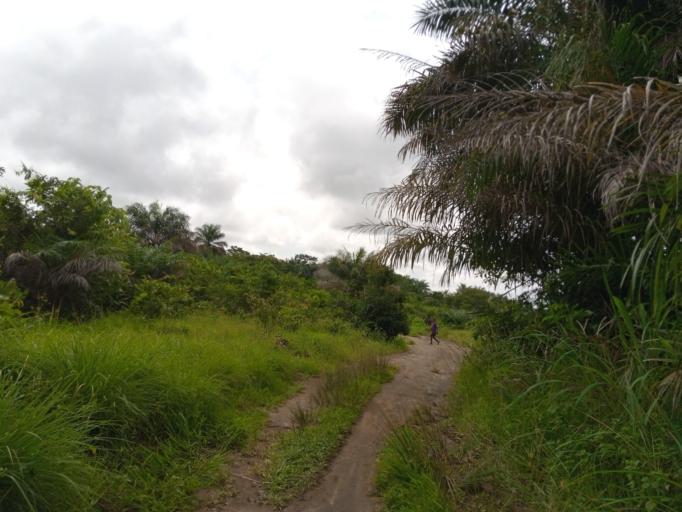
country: SL
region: Northern Province
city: Masoyila
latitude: 8.5813
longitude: -13.1867
